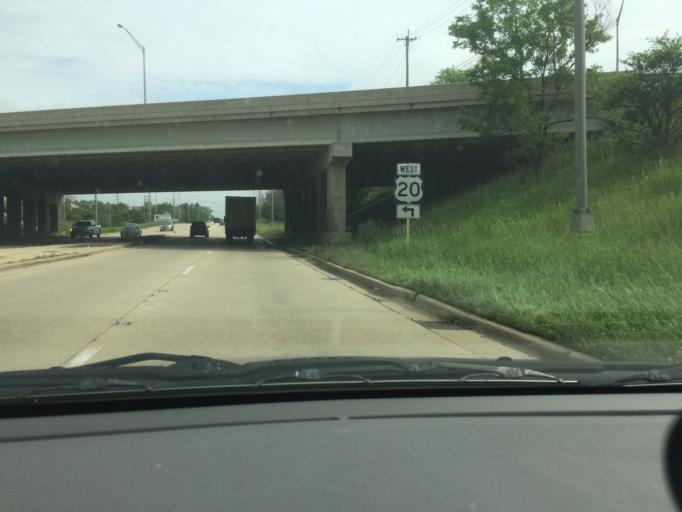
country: US
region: Illinois
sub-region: Cook County
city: Bartlett
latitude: 42.0076
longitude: -88.2032
